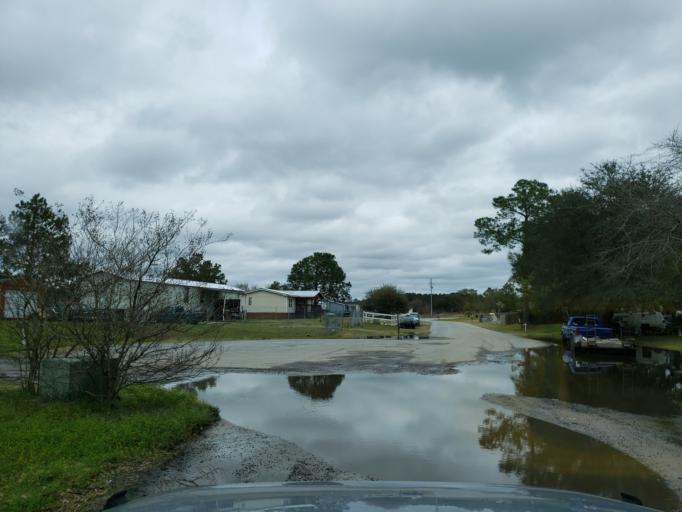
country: US
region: Georgia
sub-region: Chatham County
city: Bloomingdale
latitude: 32.0760
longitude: -81.3733
